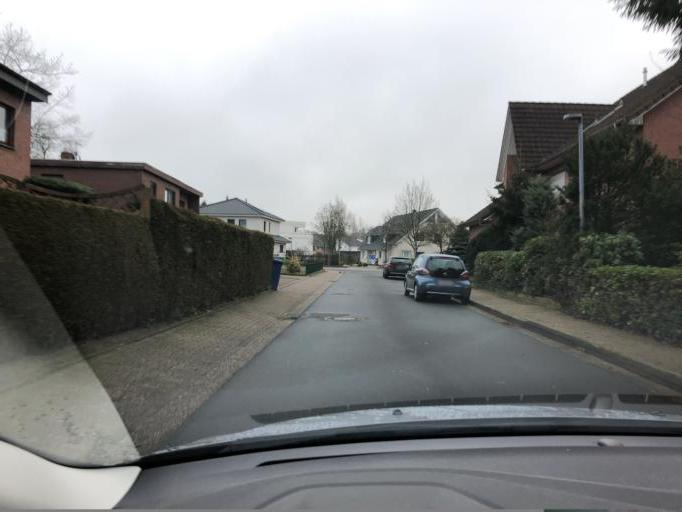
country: DE
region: Lower Saxony
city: Bad Zwischenahn
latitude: 53.1781
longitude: 8.0115
